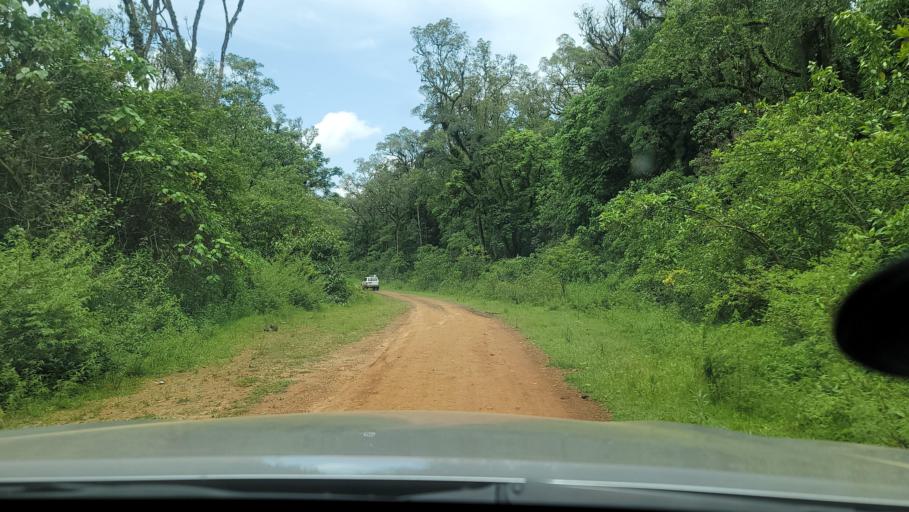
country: ET
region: Southern Nations, Nationalities, and People's Region
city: Bonga
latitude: 7.6562
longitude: 36.2474
